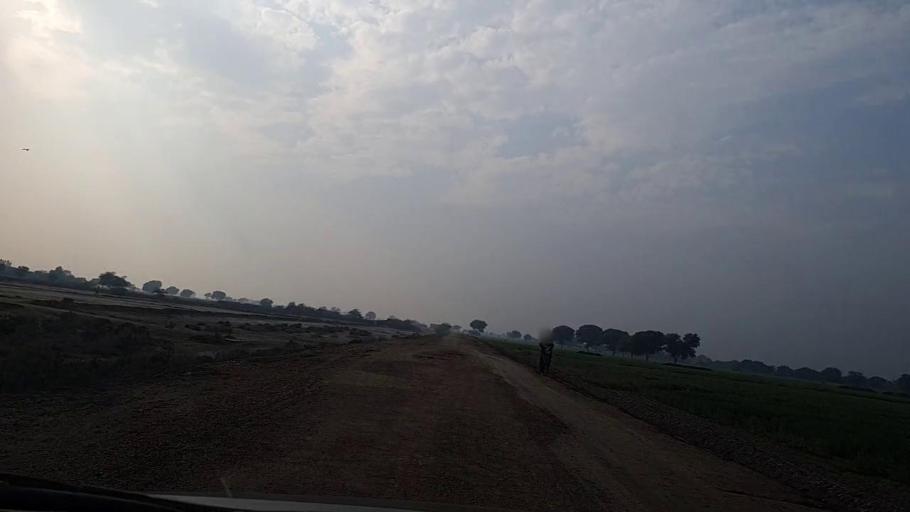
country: PK
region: Sindh
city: Nawabshah
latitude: 26.2738
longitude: 68.3369
